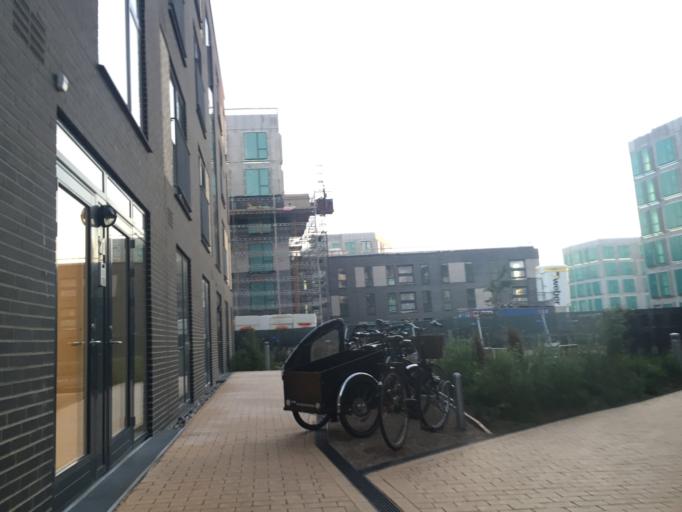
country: DK
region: Capital Region
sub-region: Kobenhavn
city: Christianshavn
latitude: 55.7039
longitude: 12.5957
